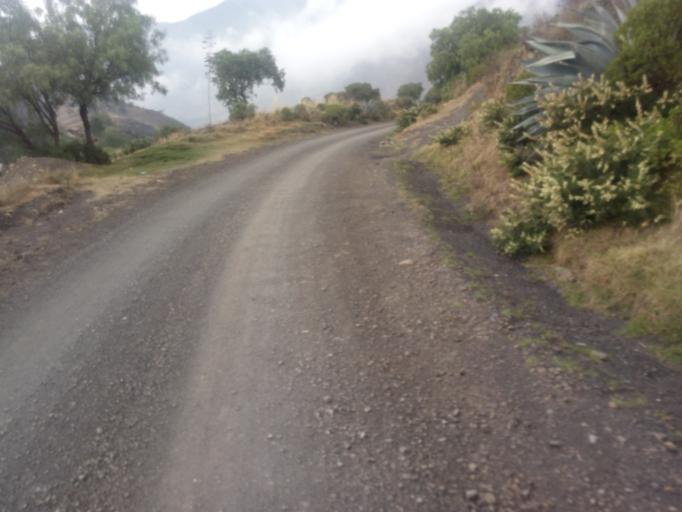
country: CO
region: Boyaca
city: Chita
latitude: 6.1932
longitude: -72.4884
